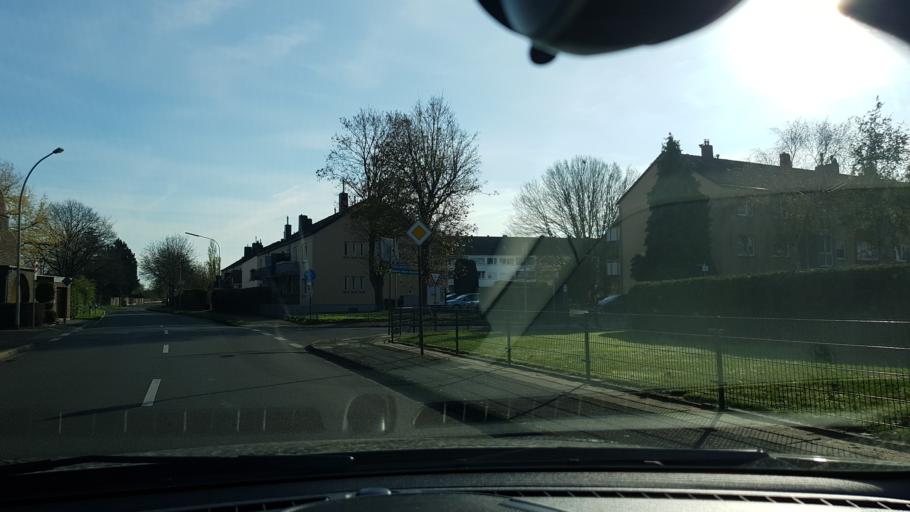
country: DE
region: North Rhine-Westphalia
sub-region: Regierungsbezirk Dusseldorf
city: Neubrueck
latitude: 51.1040
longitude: 6.6227
